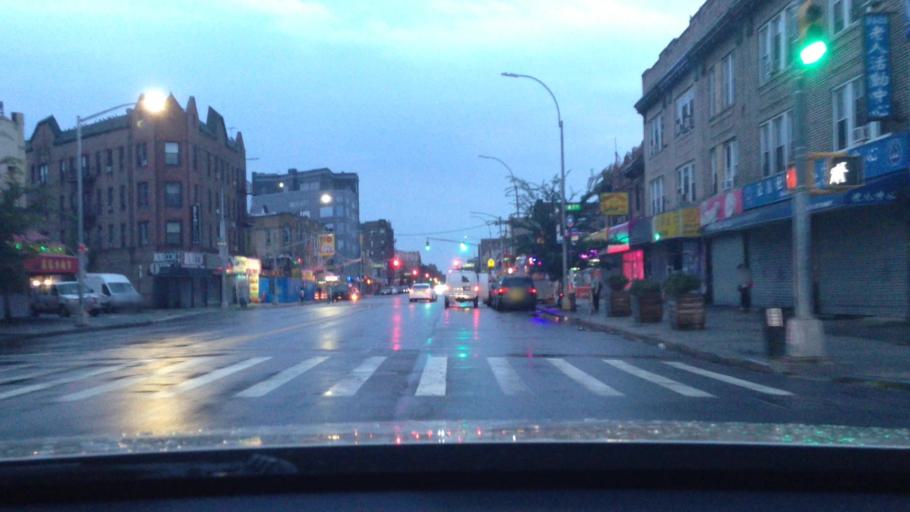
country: US
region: New York
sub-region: Kings County
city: Bensonhurst
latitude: 40.6139
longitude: -73.9815
